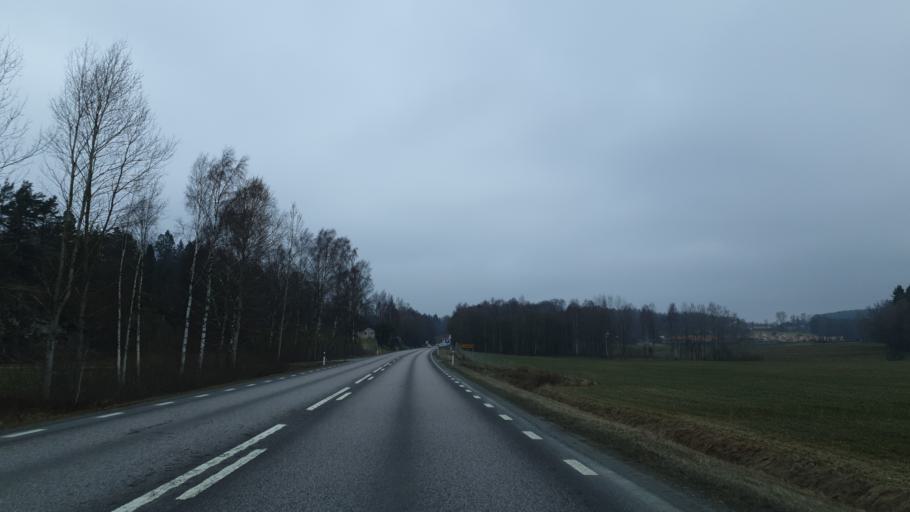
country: SE
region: Vaestra Goetaland
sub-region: Harryda Kommun
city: Ravlanda
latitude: 57.6092
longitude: 12.4364
